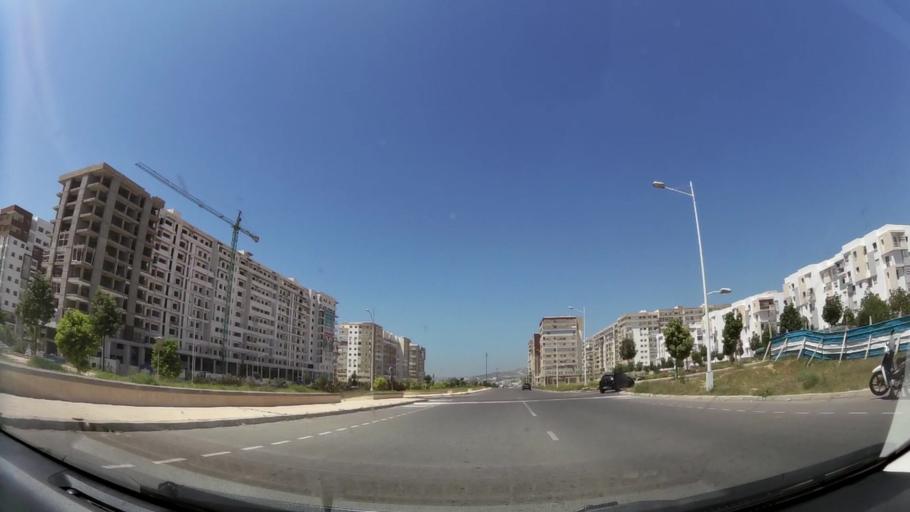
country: MA
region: Oued ed Dahab-Lagouira
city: Dakhla
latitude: 30.4362
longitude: -9.5606
